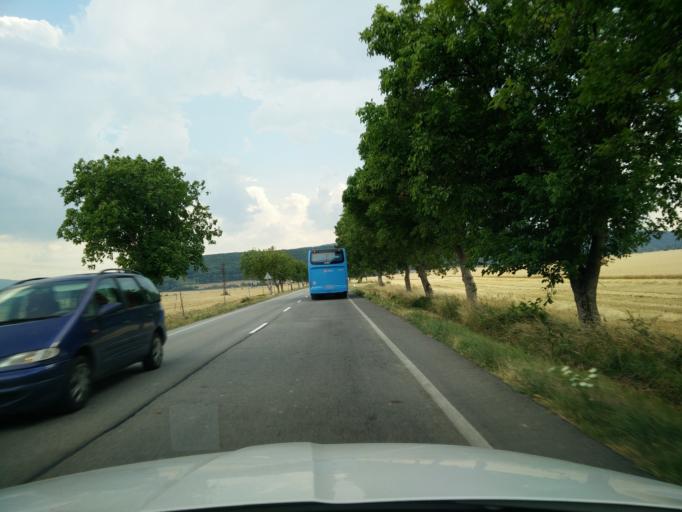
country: SK
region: Nitriansky
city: Novaky
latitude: 48.7332
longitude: 18.5002
